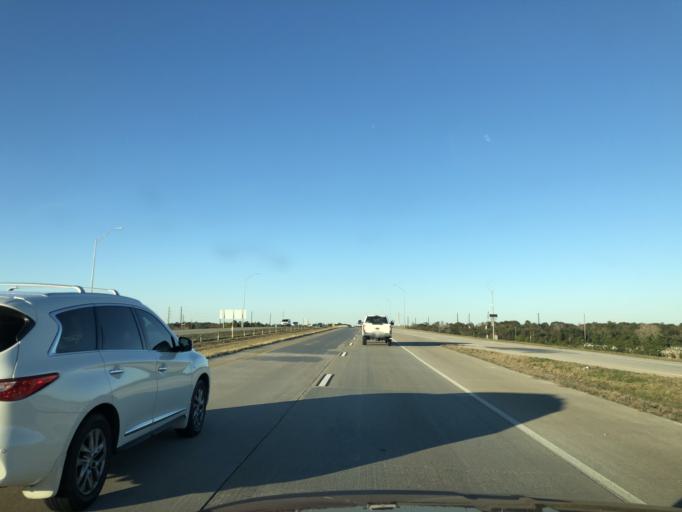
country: US
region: Texas
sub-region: Harris County
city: Cypress
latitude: 30.0181
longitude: -95.7683
